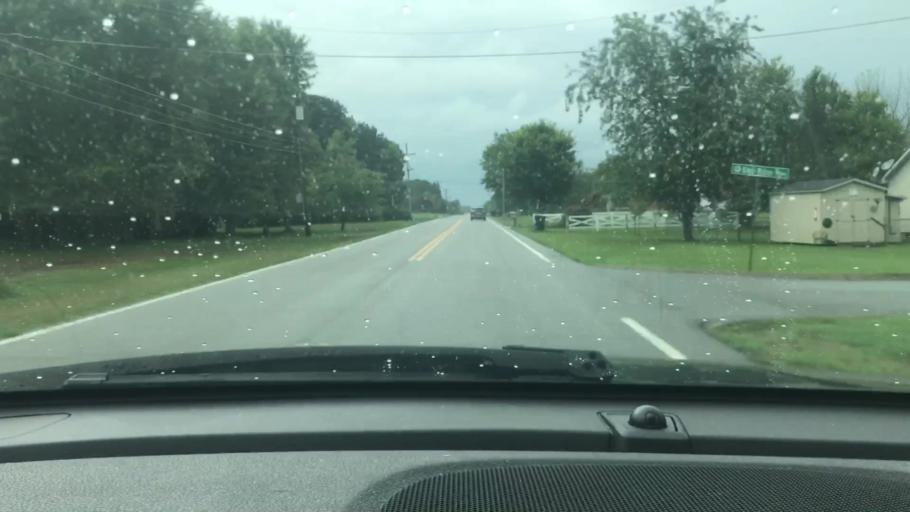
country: US
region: Tennessee
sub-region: Sumner County
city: Millersville
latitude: 36.4086
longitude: -86.6986
